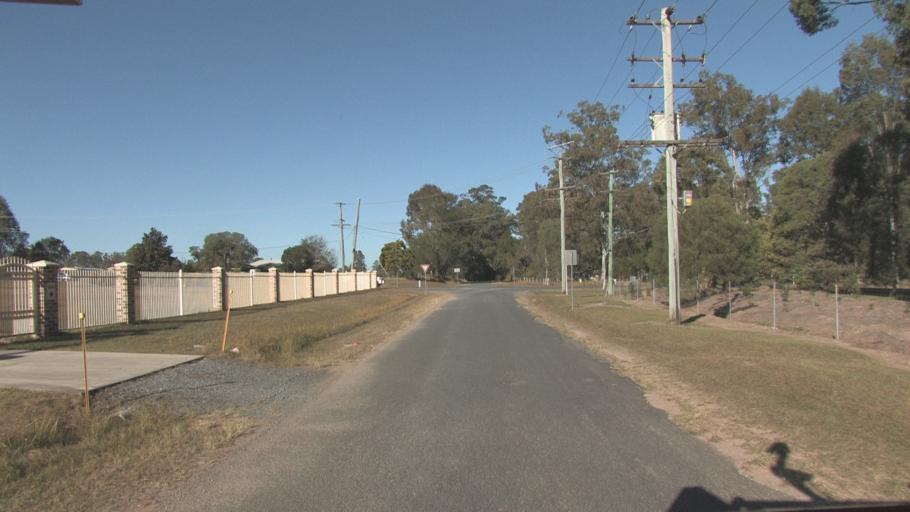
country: AU
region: Queensland
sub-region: Logan
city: North Maclean
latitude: -27.7577
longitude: 153.0333
